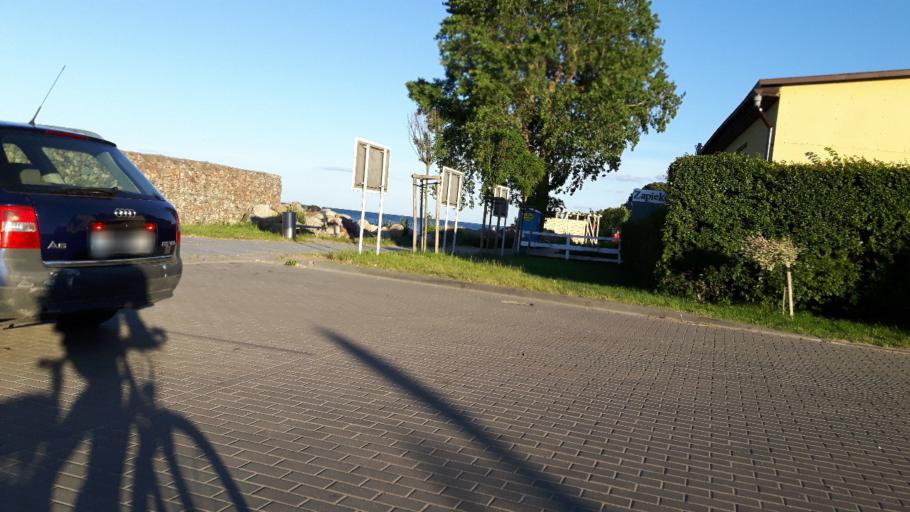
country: PL
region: Pomeranian Voivodeship
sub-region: Powiat pucki
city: Mosty
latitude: 54.6096
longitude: 18.5137
